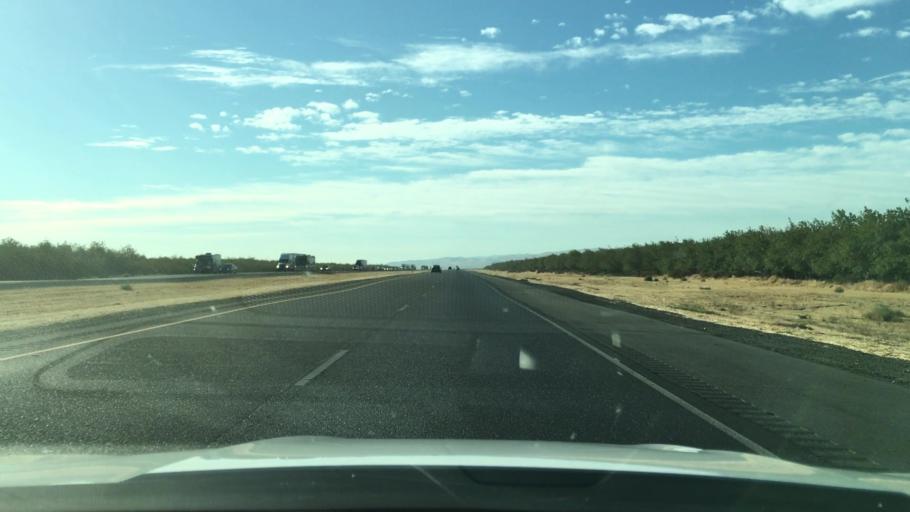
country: US
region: California
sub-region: Merced County
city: South Dos Palos
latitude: 36.7578
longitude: -120.7106
